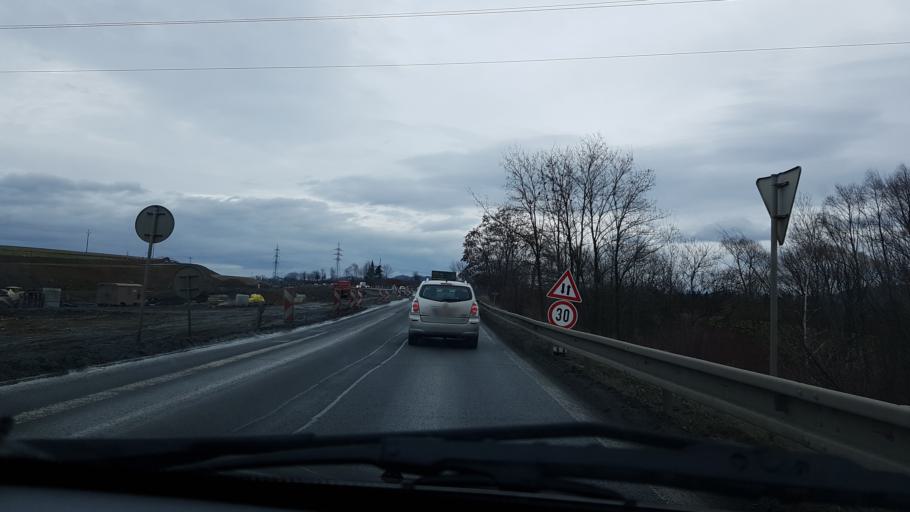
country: CZ
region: Moravskoslezsky
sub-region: Okres Novy Jicin
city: Pribor
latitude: 49.6425
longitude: 18.1620
